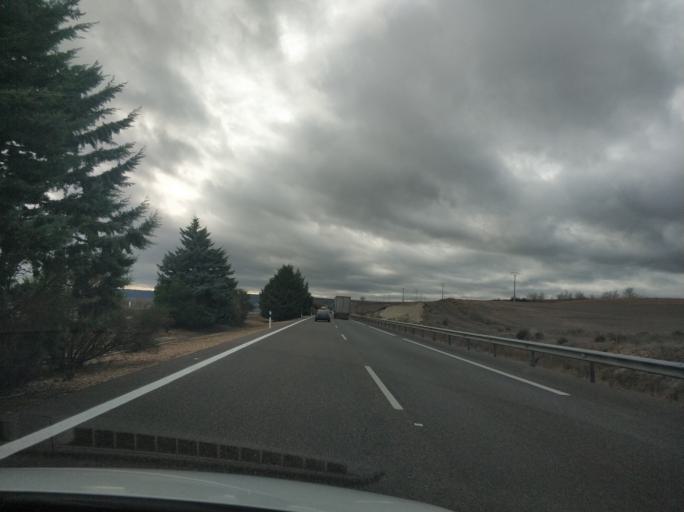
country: ES
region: Castille and Leon
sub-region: Provincia de Palencia
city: Venta de Banos
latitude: 41.9454
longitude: -4.4766
